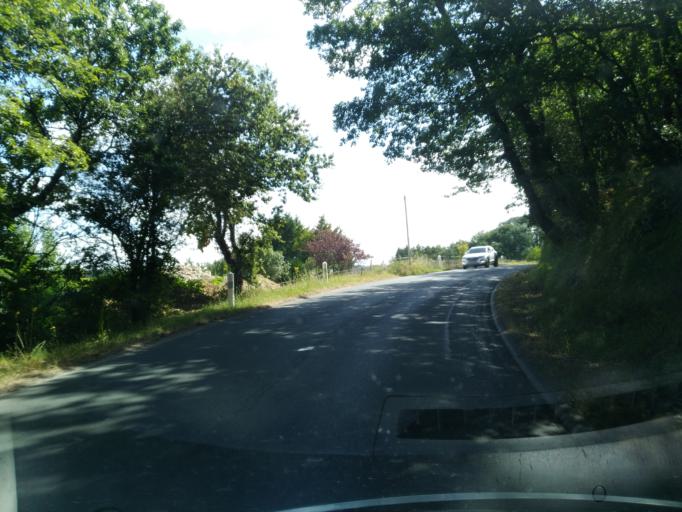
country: FR
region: Poitou-Charentes
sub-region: Departement de la Charente-Maritime
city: Vaux-sur-Mer
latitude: 45.6658
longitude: -1.0756
